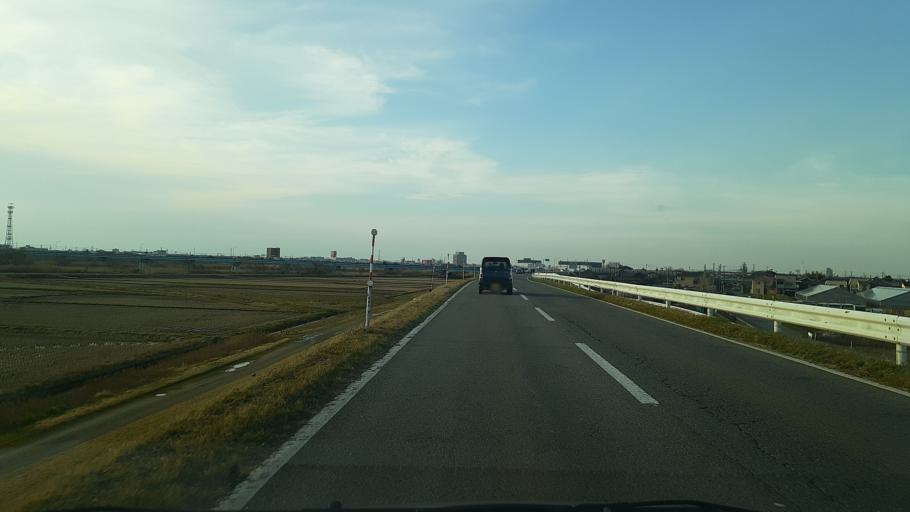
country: JP
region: Niigata
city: Niigata-shi
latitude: 37.8509
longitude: 139.0266
